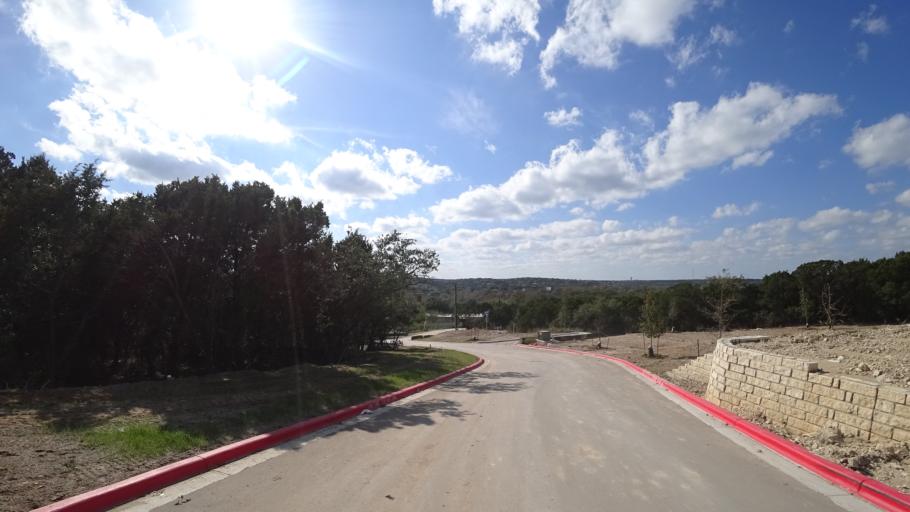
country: US
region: Texas
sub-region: Travis County
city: Barton Creek
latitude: 30.2458
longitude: -97.8779
